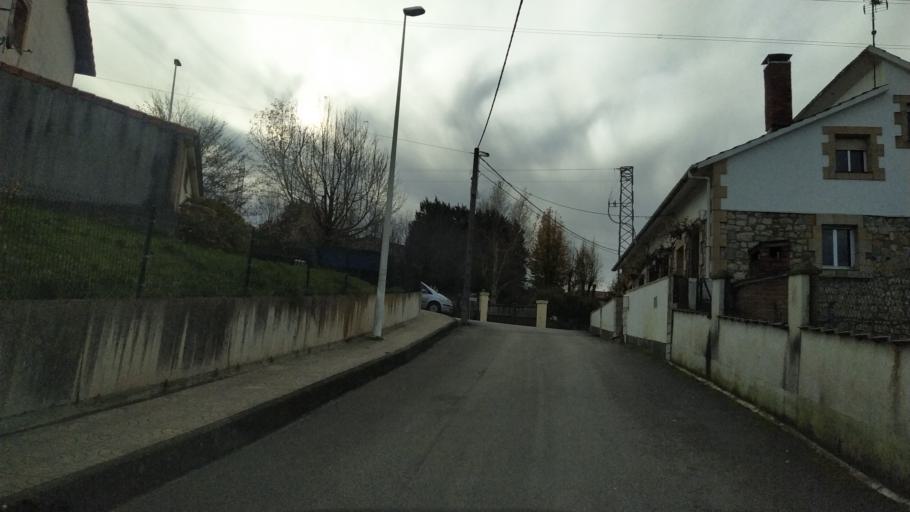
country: ES
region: Cantabria
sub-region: Provincia de Cantabria
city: Reocin
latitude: 43.3553
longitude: -4.0882
